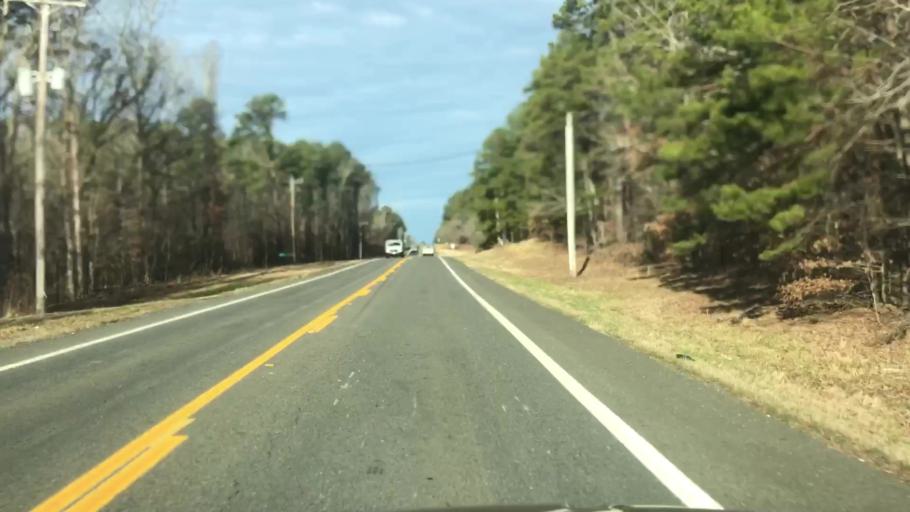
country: US
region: Arkansas
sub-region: Montgomery County
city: Mount Ida
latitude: 34.5410
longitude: -93.6076
